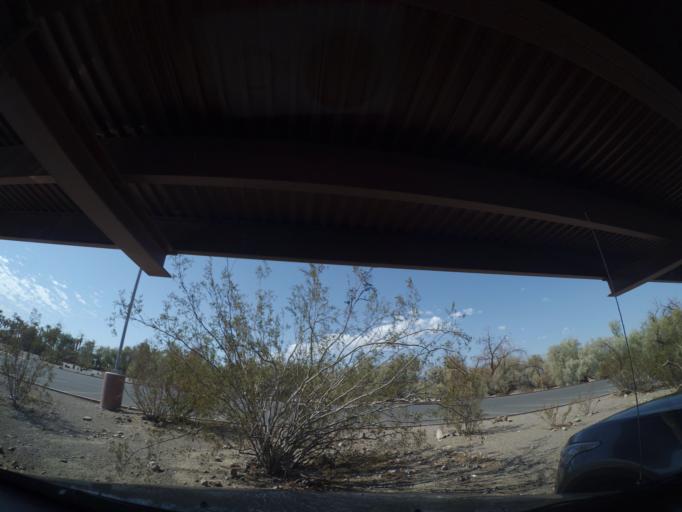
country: US
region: Nevada
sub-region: Nye County
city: Beatty
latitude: 36.4614
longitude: -116.8670
